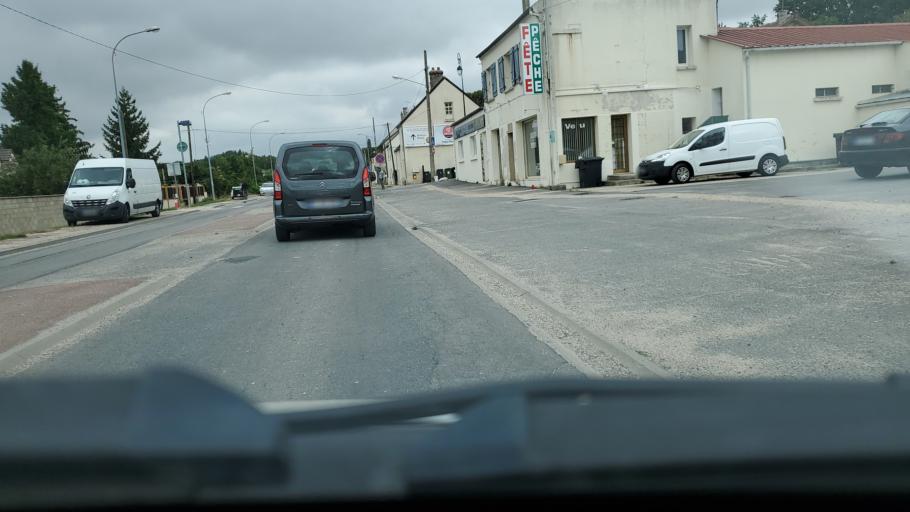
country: FR
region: Ile-de-France
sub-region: Departement de Seine-et-Marne
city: Mouroux
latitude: 48.8214
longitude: 3.0463
